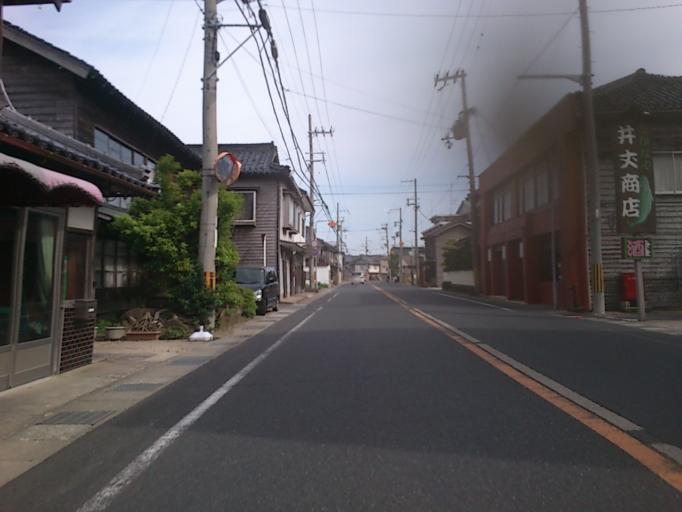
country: JP
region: Kyoto
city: Miyazu
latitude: 35.6865
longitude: 135.0230
